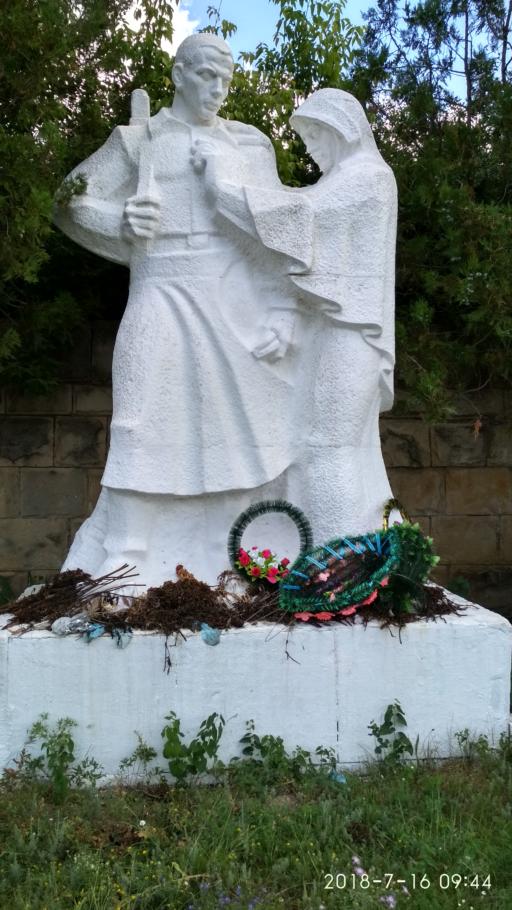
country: MD
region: Telenesti
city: Cocieri
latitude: 47.3122
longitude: 28.9751
